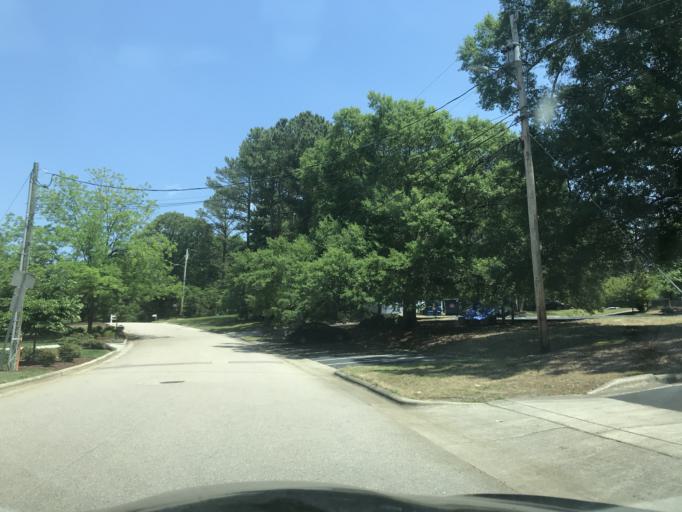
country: US
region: North Carolina
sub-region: Wake County
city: West Raleigh
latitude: 35.8492
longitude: -78.6459
